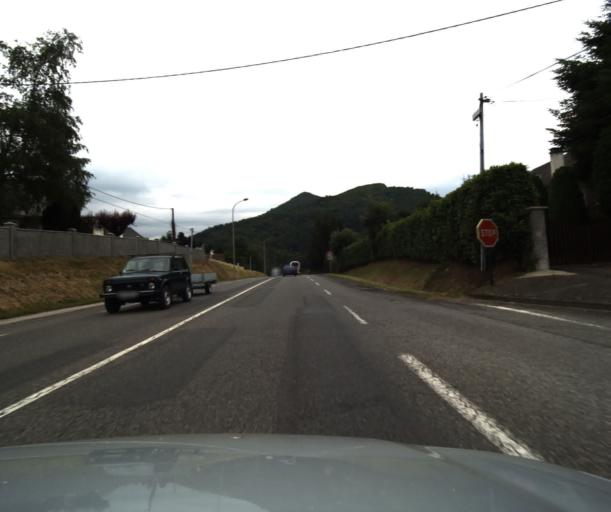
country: FR
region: Midi-Pyrenees
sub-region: Departement des Hautes-Pyrenees
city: Lourdes
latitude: 43.1000
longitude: -0.0298
